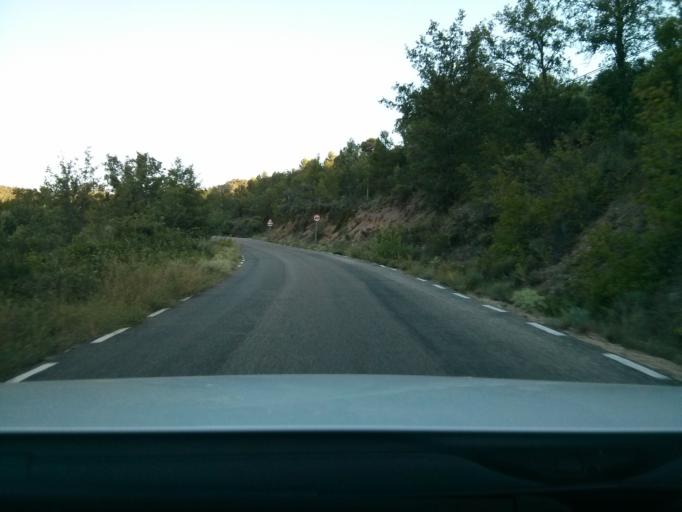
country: ES
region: Castille-La Mancha
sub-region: Provincia de Guadalajara
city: Mantiel
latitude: 40.6295
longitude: -2.6410
